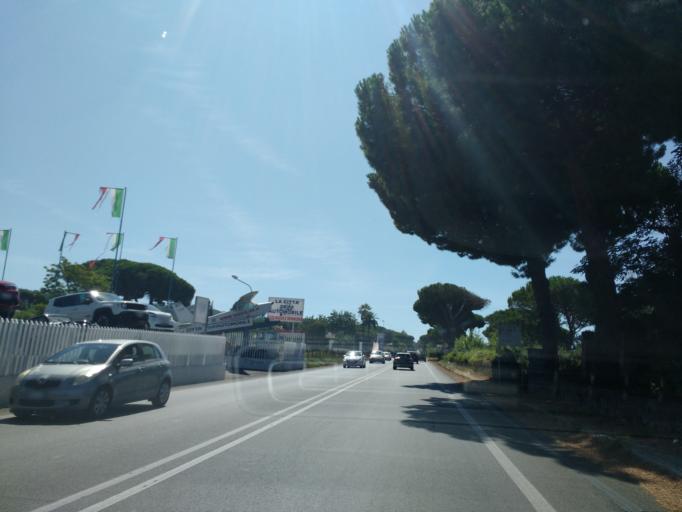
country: IT
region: Latium
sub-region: Citta metropolitana di Roma Capitale
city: Marino
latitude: 41.7548
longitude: 12.6296
